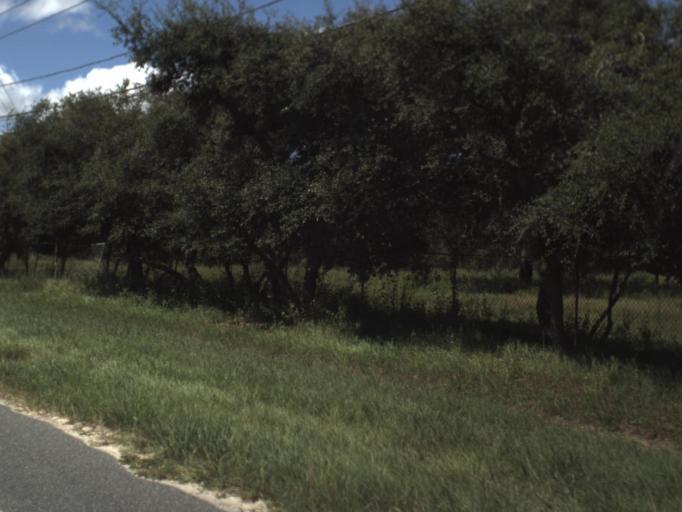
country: US
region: Florida
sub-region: Polk County
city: Davenport
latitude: 28.1784
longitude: -81.5948
